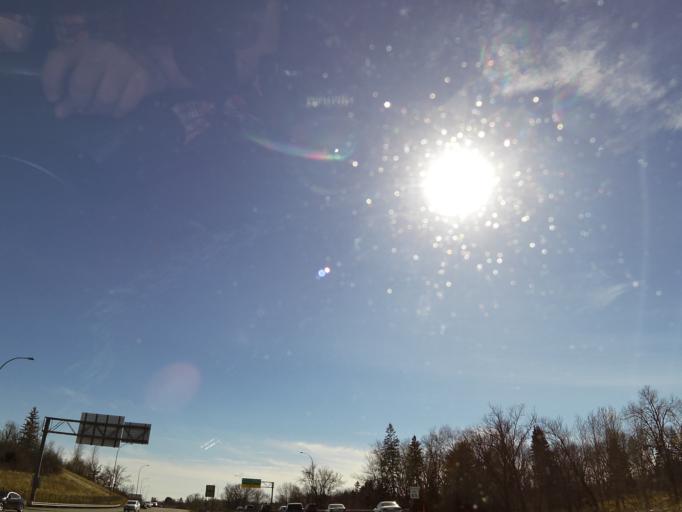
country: US
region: Minnesota
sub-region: Hennepin County
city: Edina
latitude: 44.8509
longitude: -93.3982
